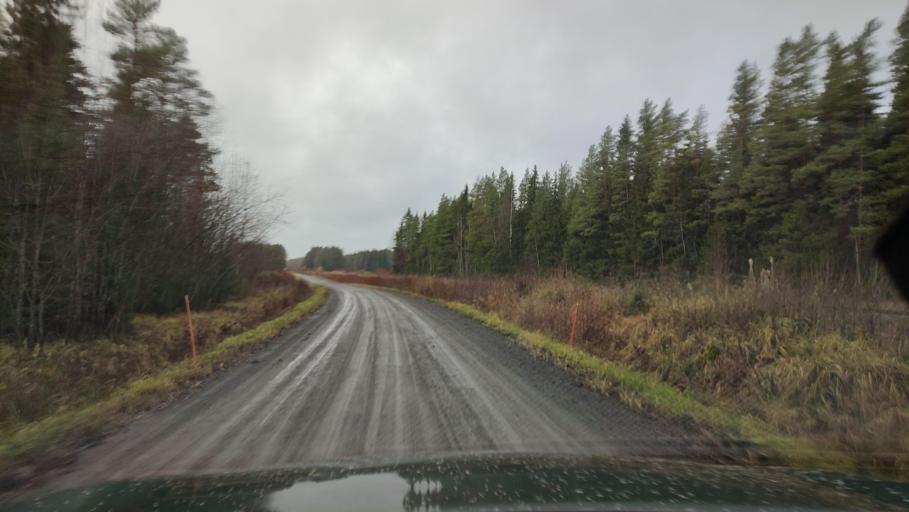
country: FI
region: Ostrobothnia
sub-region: Sydosterbotten
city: Naerpes
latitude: 62.4567
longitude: 21.5100
